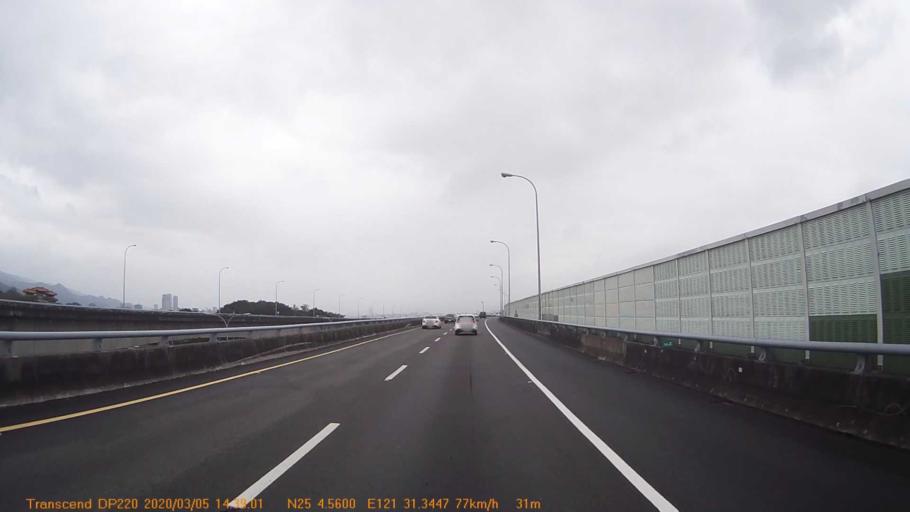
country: TW
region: Taipei
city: Taipei
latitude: 25.0747
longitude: 121.5229
